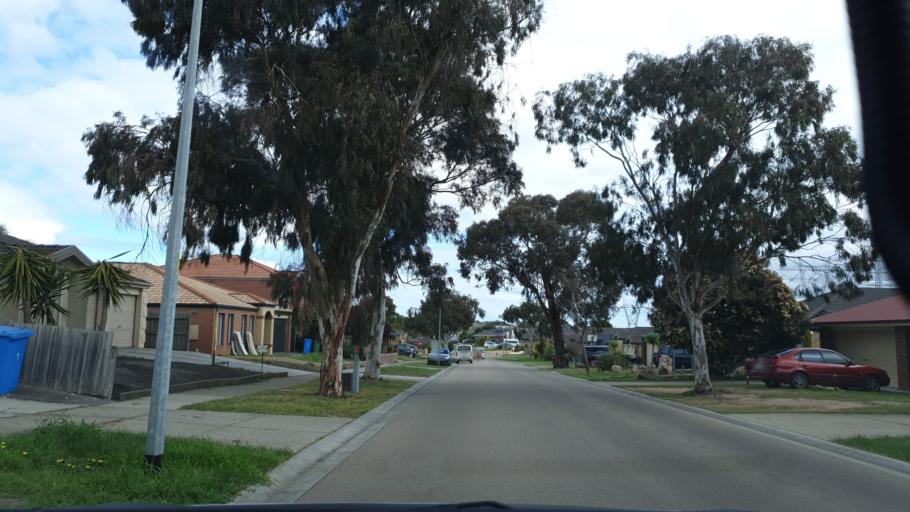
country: AU
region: Victoria
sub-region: Casey
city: Narre Warren South
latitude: -38.0515
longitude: 145.2835
